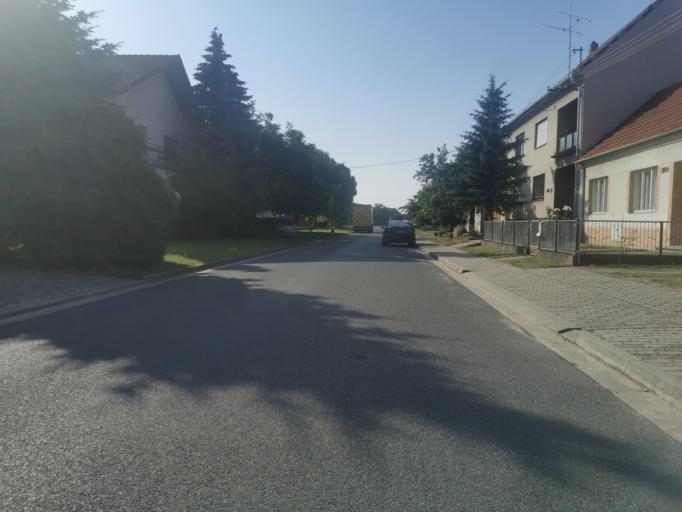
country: CZ
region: South Moravian
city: Vacenovice
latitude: 48.9412
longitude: 17.1786
